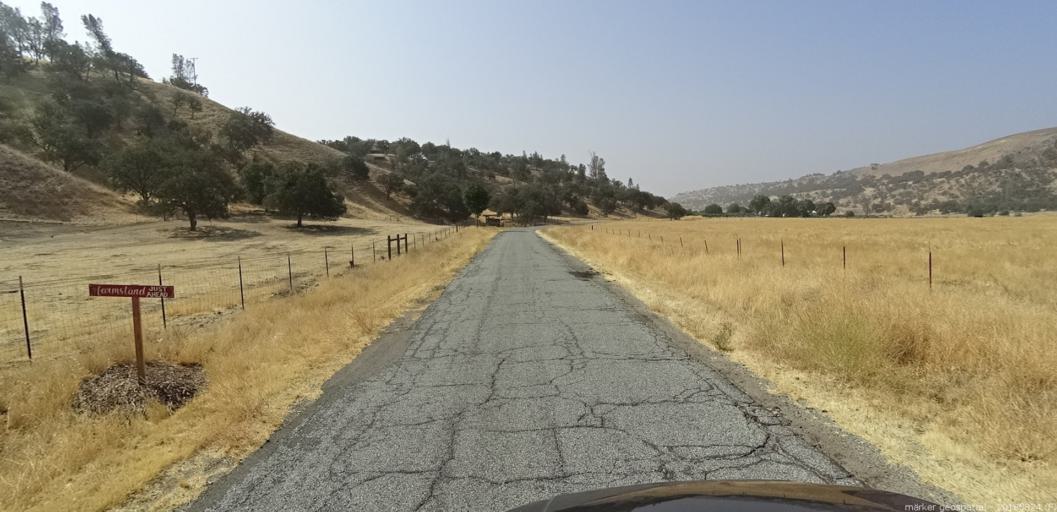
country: US
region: California
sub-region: San Luis Obispo County
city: San Miguel
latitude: 35.8777
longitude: -120.6996
